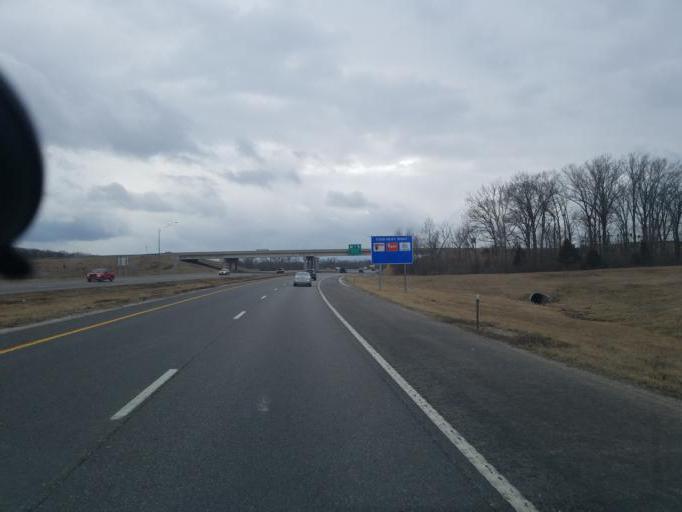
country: US
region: Missouri
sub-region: Boone County
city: Columbia
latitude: 38.9784
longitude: -92.2817
